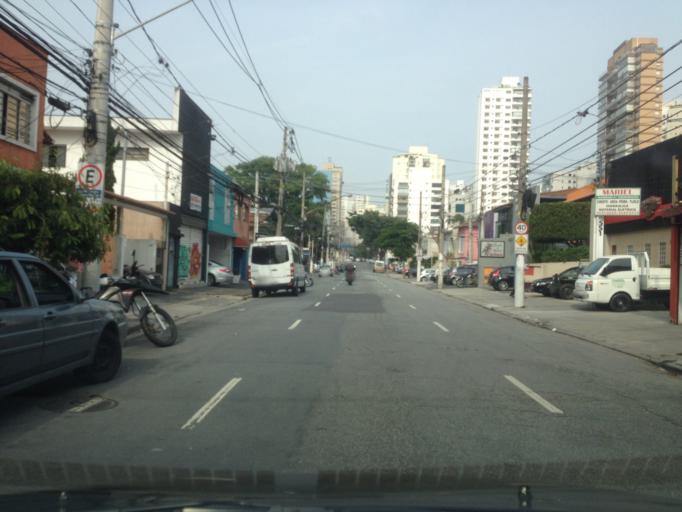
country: BR
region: Sao Paulo
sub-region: Sao Paulo
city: Sao Paulo
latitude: -23.5916
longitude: -46.6778
